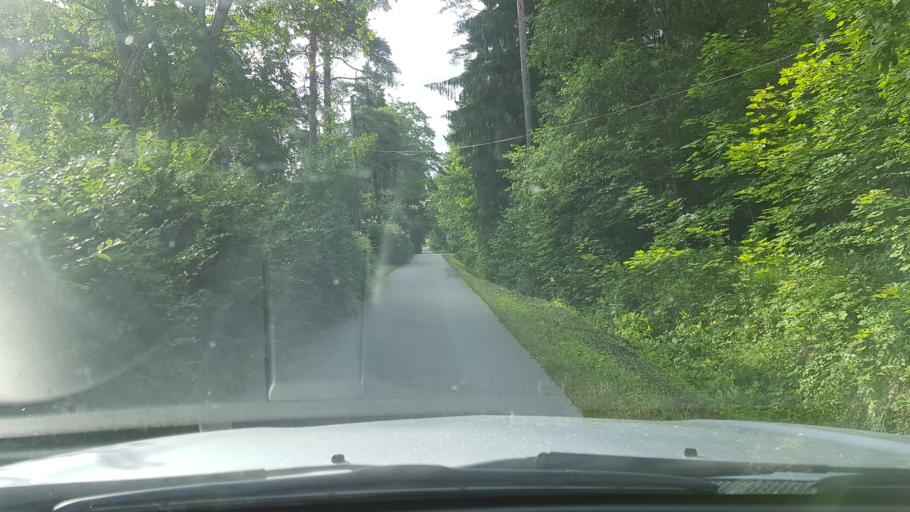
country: EE
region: Ida-Virumaa
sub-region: Narva-Joesuu linn
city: Narva-Joesuu
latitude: 59.4548
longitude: 28.0299
